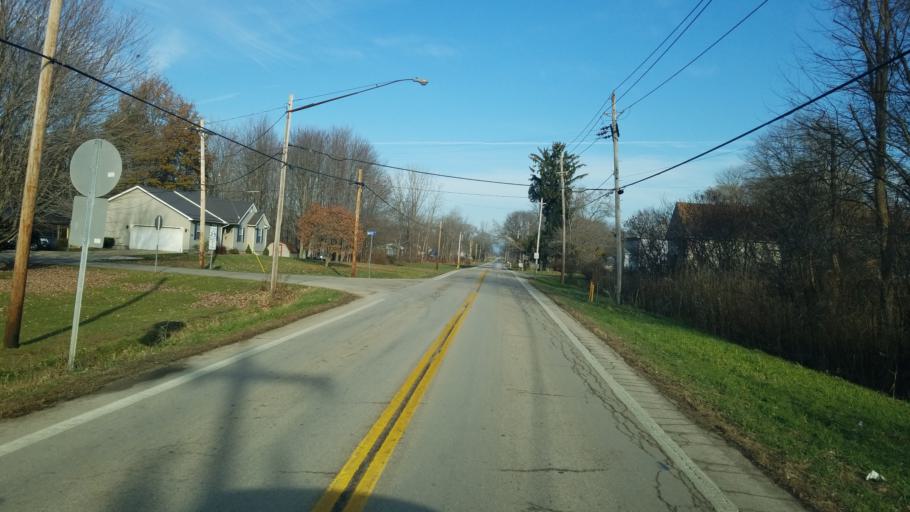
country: US
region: Ohio
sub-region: Ashtabula County
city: North Kingsville
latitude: 41.9092
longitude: -80.6919
